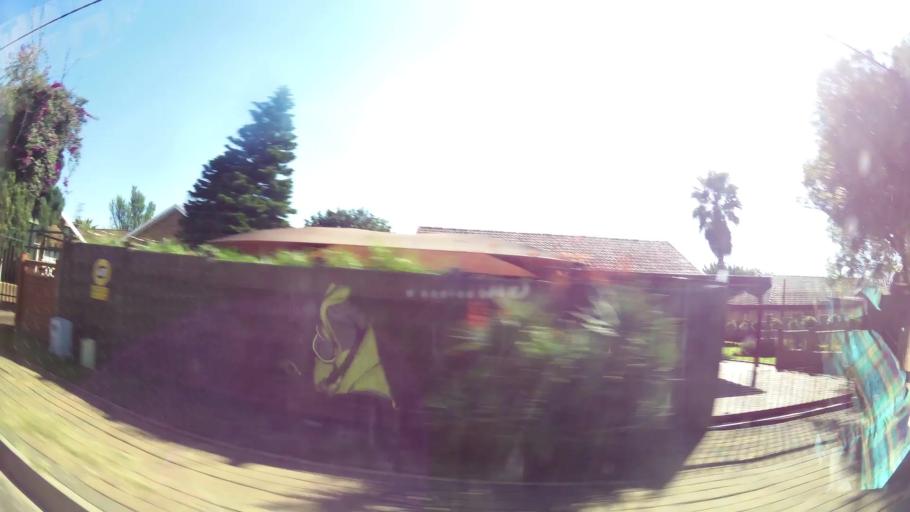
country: ZA
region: Gauteng
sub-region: City of Tshwane Metropolitan Municipality
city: Centurion
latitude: -25.8415
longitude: 28.2091
